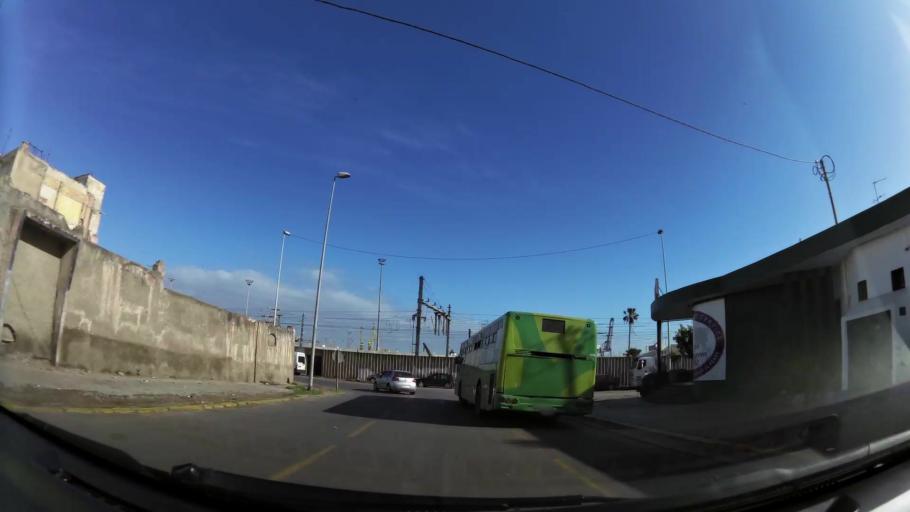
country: MA
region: Grand Casablanca
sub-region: Casablanca
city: Casablanca
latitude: 33.5974
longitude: -7.6062
